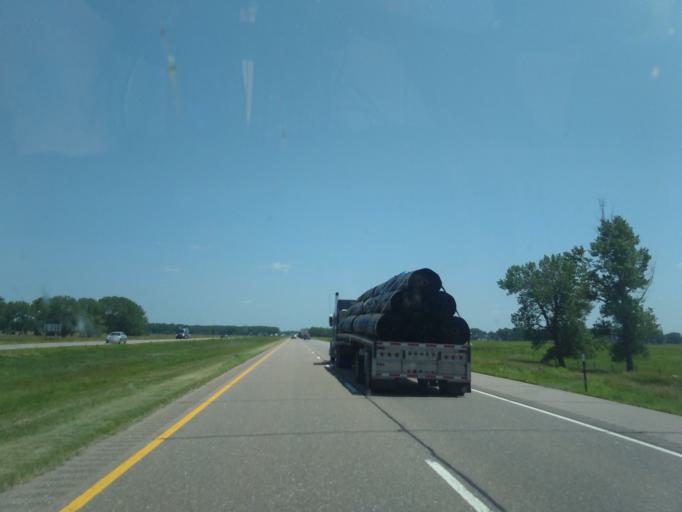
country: US
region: Nebraska
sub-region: Dawson County
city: Gothenburg
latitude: 40.8963
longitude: -100.1214
